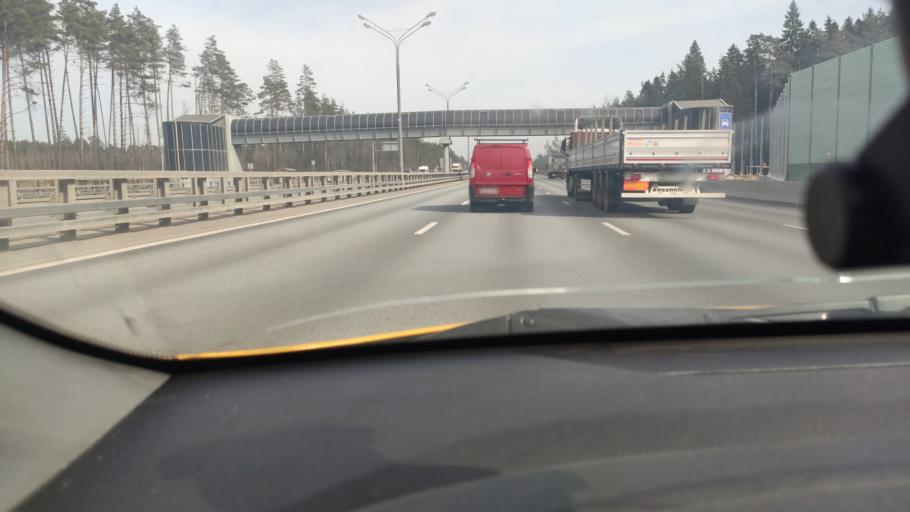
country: RU
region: Moskovskaya
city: Zhavoronki
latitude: 55.6173
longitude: 37.1075
